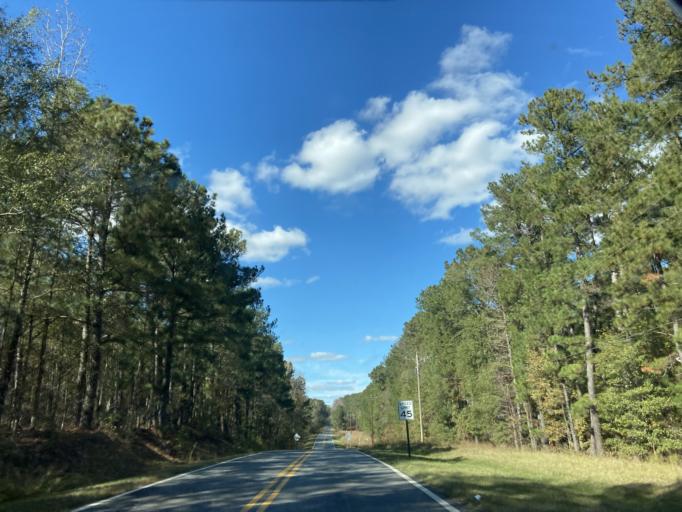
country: US
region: Georgia
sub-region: Jones County
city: Gray
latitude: 32.9312
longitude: -83.5023
